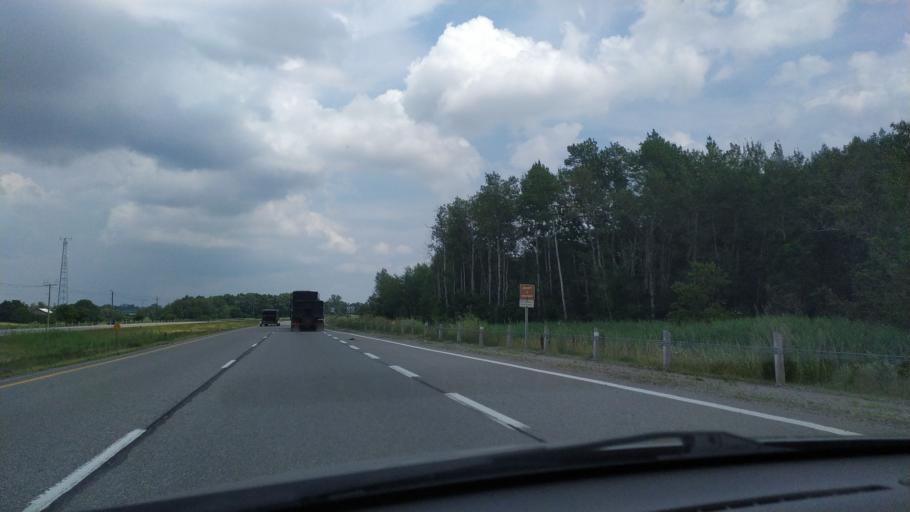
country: CA
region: Ontario
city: Kitchener
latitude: 43.4065
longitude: -80.5931
